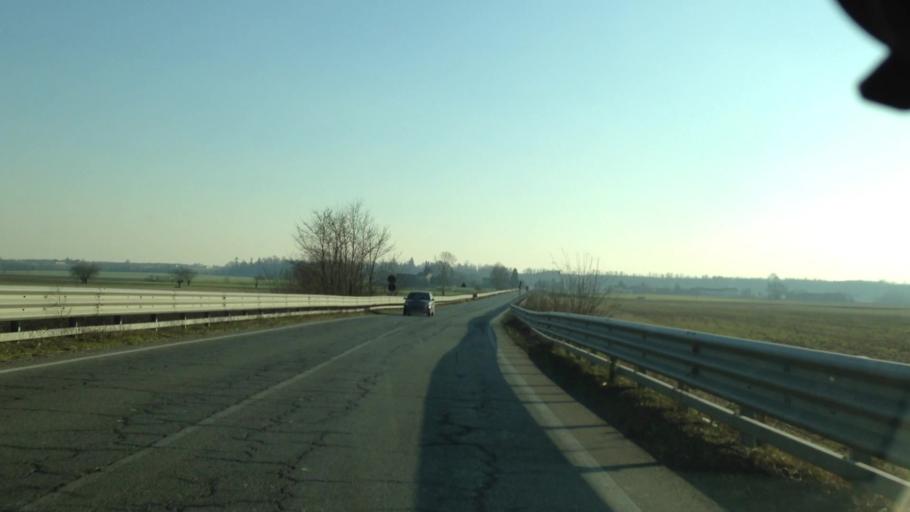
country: IT
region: Piedmont
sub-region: Provincia di Alessandria
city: Felizzano
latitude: 44.8883
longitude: 8.4402
